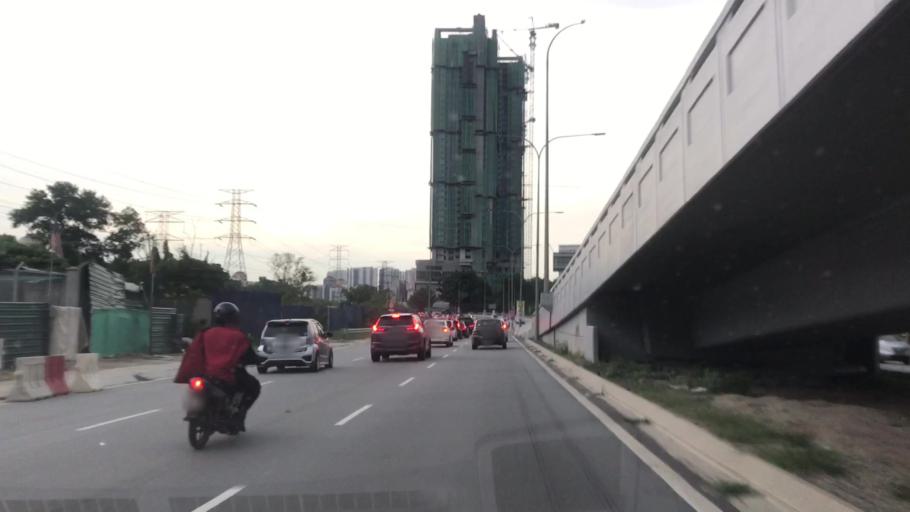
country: MY
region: Selangor
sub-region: Petaling
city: Petaling Jaya
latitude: 3.0528
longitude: 101.6685
